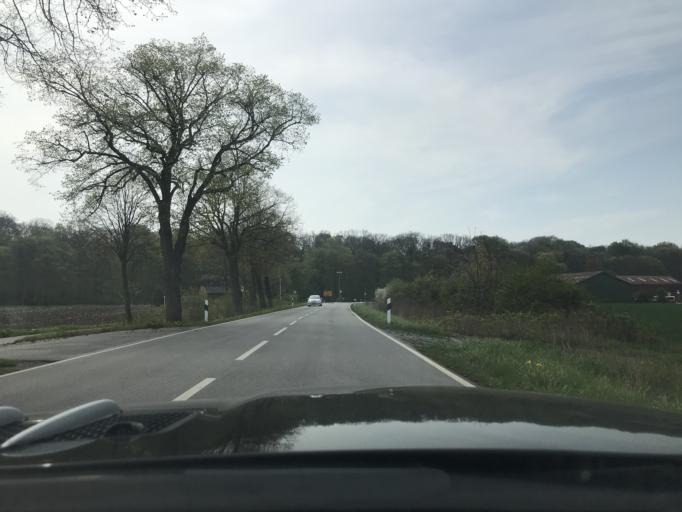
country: DE
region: Schleswig-Holstein
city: Grube
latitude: 54.2083
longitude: 11.0391
